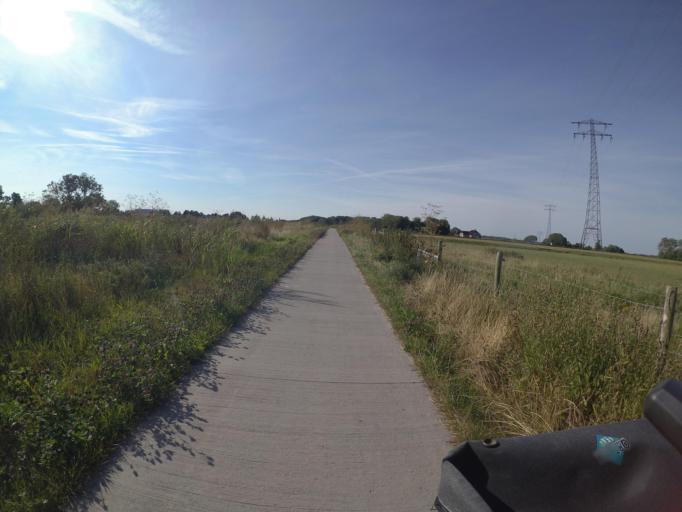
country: NL
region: Friesland
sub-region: Gemeente Dongeradeel
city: Dokkum
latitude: 53.3234
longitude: 5.9775
